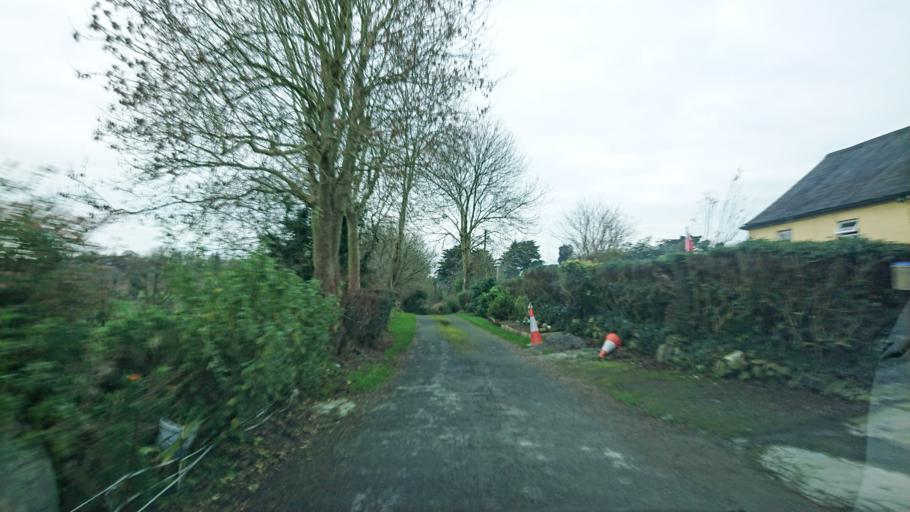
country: IE
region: Leinster
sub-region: Kilkenny
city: Mooncoin
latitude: 52.2136
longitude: -7.2711
